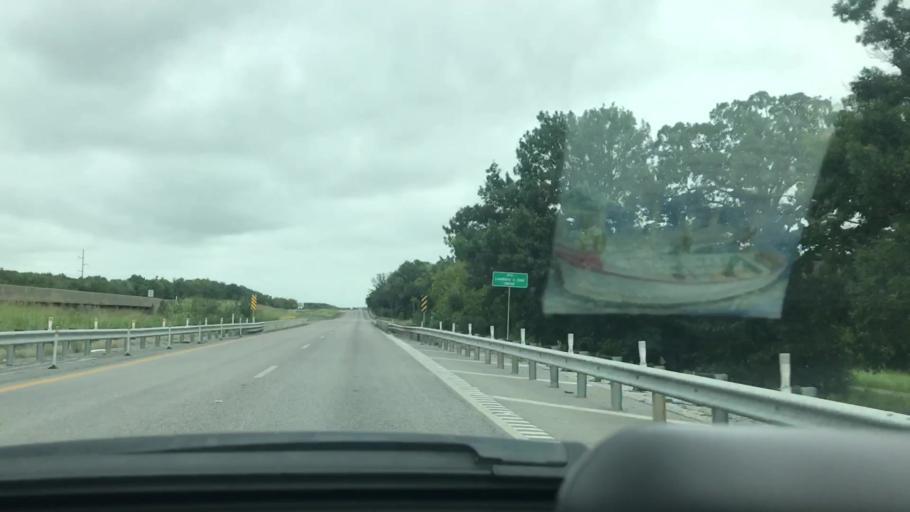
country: US
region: Oklahoma
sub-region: Coal County
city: Coalgate
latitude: 34.6256
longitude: -95.9608
